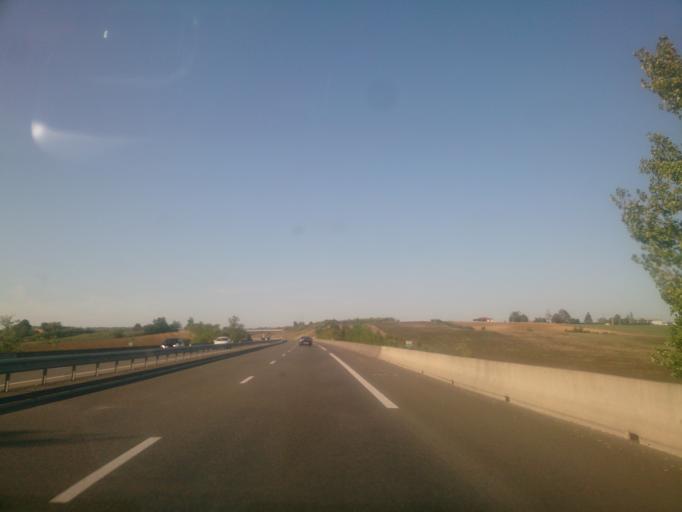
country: FR
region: Midi-Pyrenees
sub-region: Departement du Tarn-et-Garonne
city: Caussade
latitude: 44.2013
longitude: 1.5401
